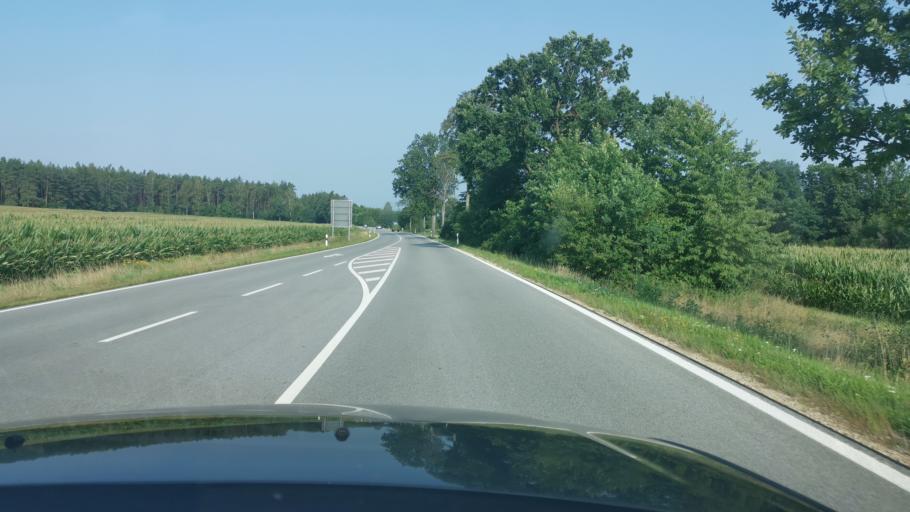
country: DE
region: Bavaria
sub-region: Upper Palatinate
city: Schnaittenbach
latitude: 49.5457
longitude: 12.0566
